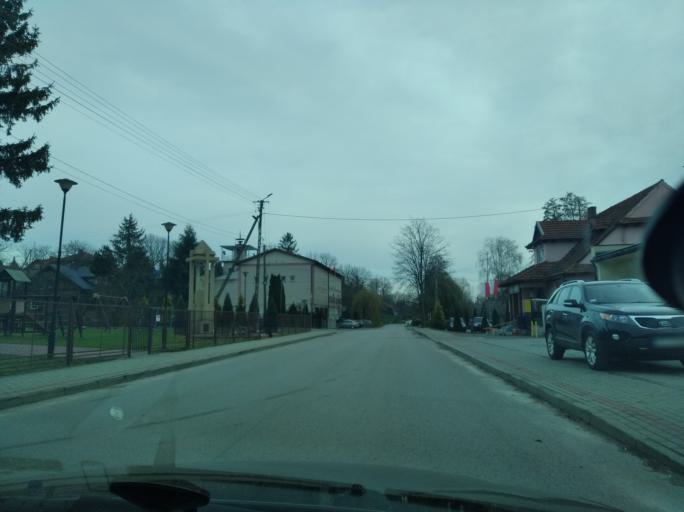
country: PL
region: Subcarpathian Voivodeship
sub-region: Powiat przeworski
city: Gac
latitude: 50.0285
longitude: 22.3659
